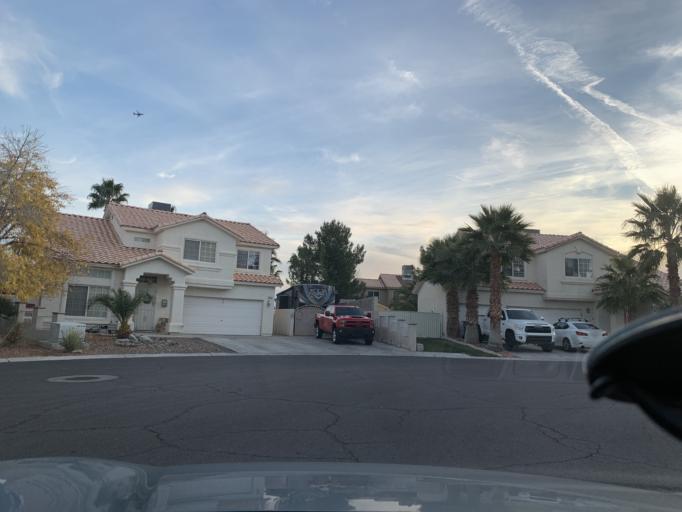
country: US
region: Nevada
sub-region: Clark County
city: Spring Valley
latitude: 36.0915
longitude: -115.2333
